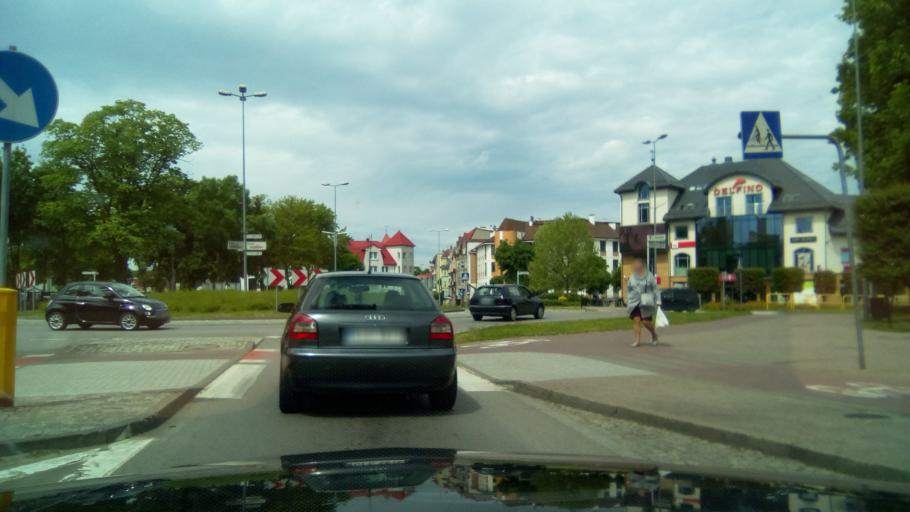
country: PL
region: Pomeranian Voivodeship
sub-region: Powiat leborski
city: Lebork
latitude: 54.5392
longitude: 17.7479
